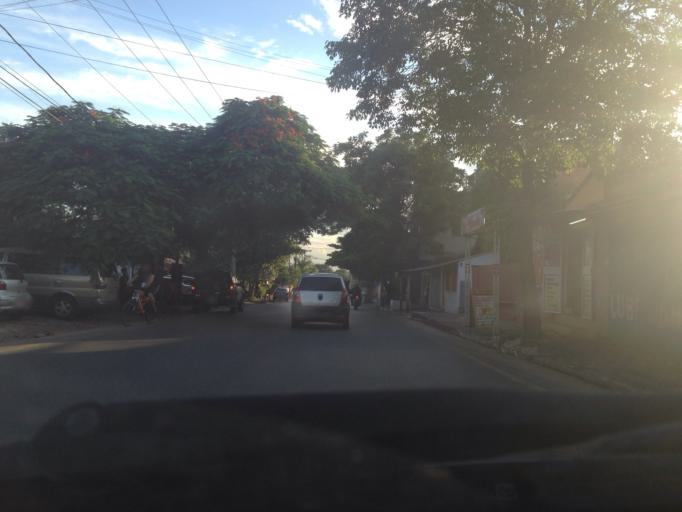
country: PY
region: Central
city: Lambare
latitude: -25.3270
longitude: -57.5834
